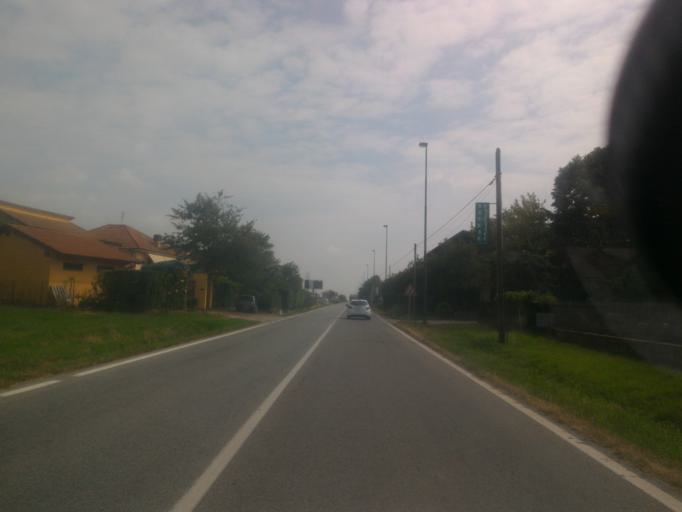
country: IT
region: Piedmont
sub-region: Provincia di Torino
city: Bricherasio
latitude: 44.8462
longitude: 7.3138
